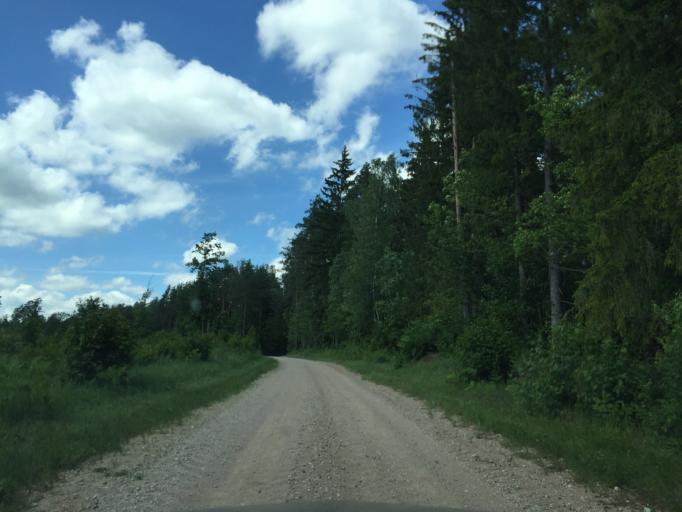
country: LV
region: Engure
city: Smarde
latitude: 56.9876
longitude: 23.2860
